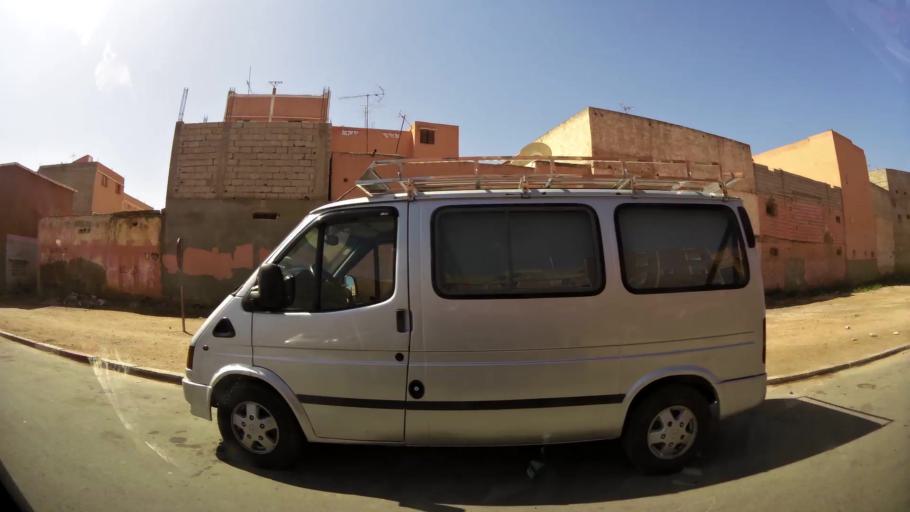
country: MA
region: Souss-Massa-Draa
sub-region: Inezgane-Ait Mellou
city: Inezgane
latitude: 30.3459
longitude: -9.5056
